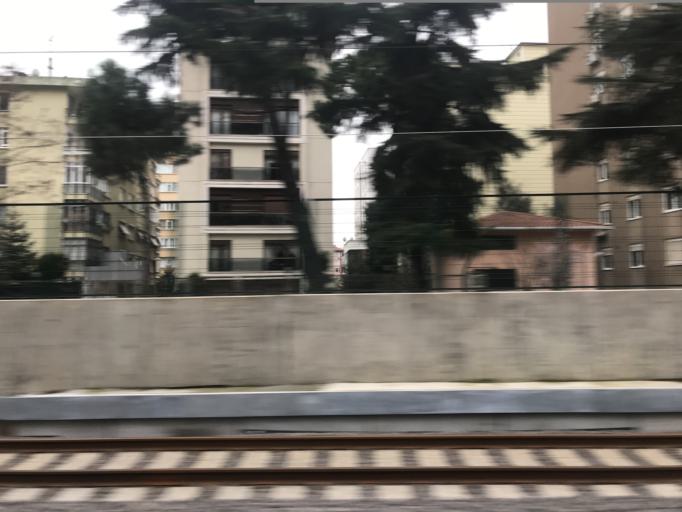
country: TR
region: Istanbul
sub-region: Atasehir
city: Atasehir
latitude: 40.9771
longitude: 29.0699
